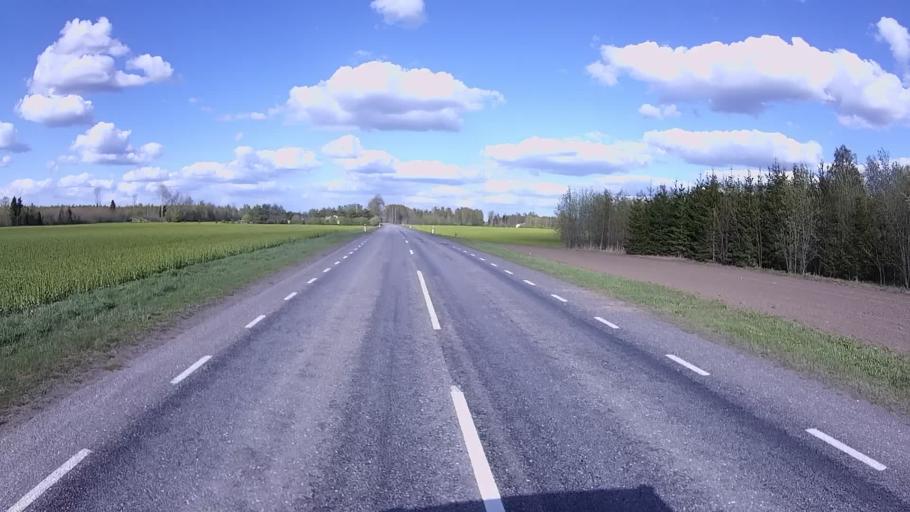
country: EE
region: Jogevamaa
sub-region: Poltsamaa linn
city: Poltsamaa
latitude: 58.7034
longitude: 26.1552
